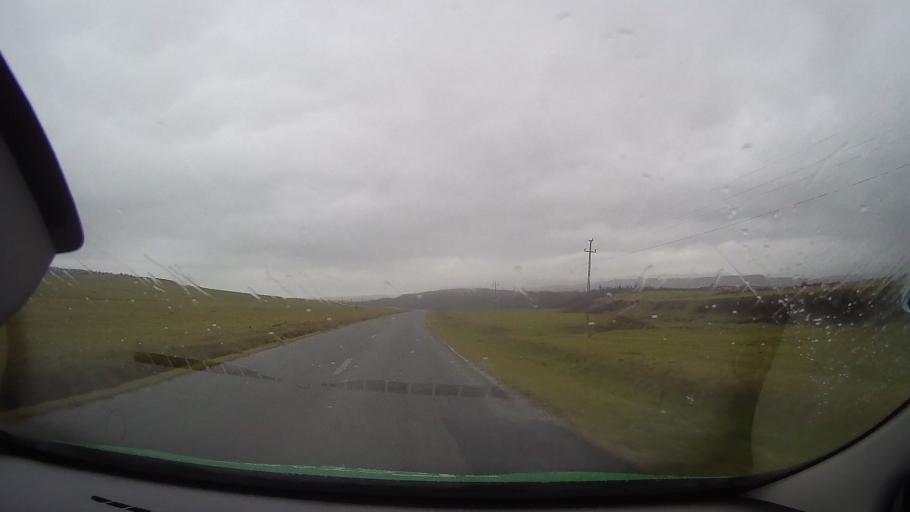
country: RO
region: Mures
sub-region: Comuna Brancovenesti
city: Valenii de Mures
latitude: 46.9077
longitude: 24.7841
